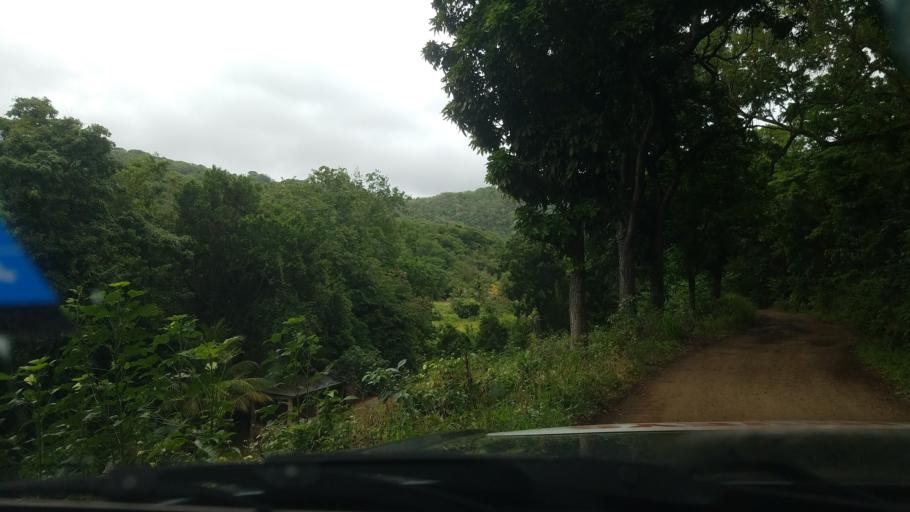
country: LC
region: Gros-Islet
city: Gros Islet
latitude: 14.0215
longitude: -60.9154
